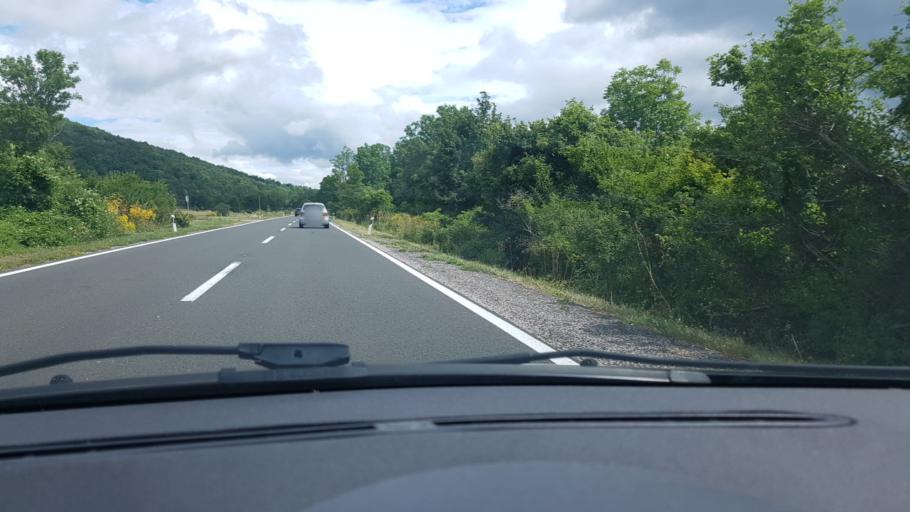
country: HR
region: Zadarska
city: Gracac
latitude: 44.4825
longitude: 15.7762
